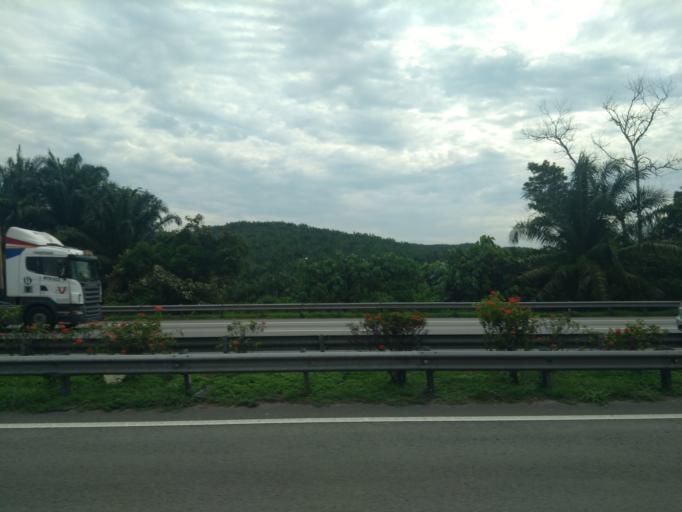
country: MY
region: Negeri Sembilan
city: Seremban
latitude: 2.6499
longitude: 101.9916
